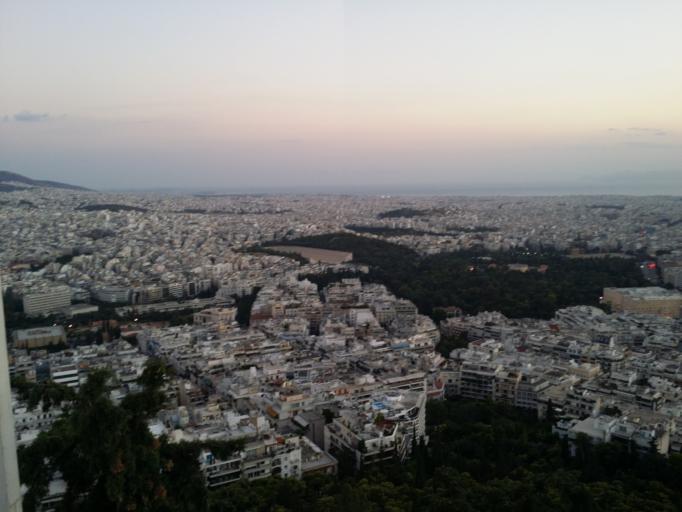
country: GR
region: Attica
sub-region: Nomarchia Athinas
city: Kipseli
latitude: 37.9818
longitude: 23.7432
